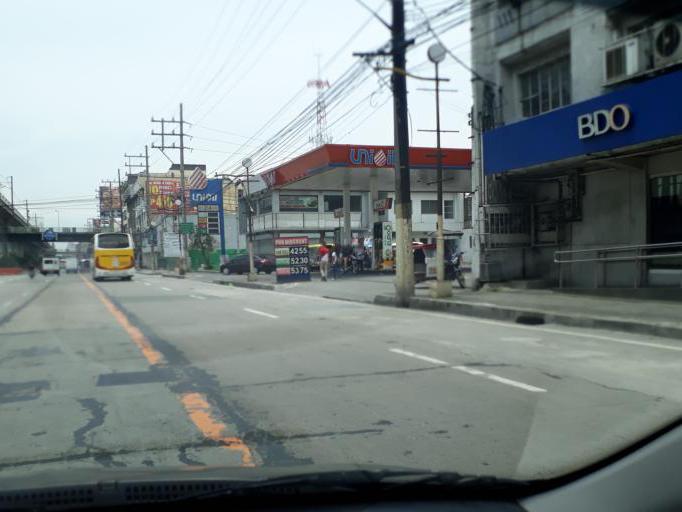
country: PH
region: Calabarzon
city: Del Monte
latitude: 14.6576
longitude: 120.9909
